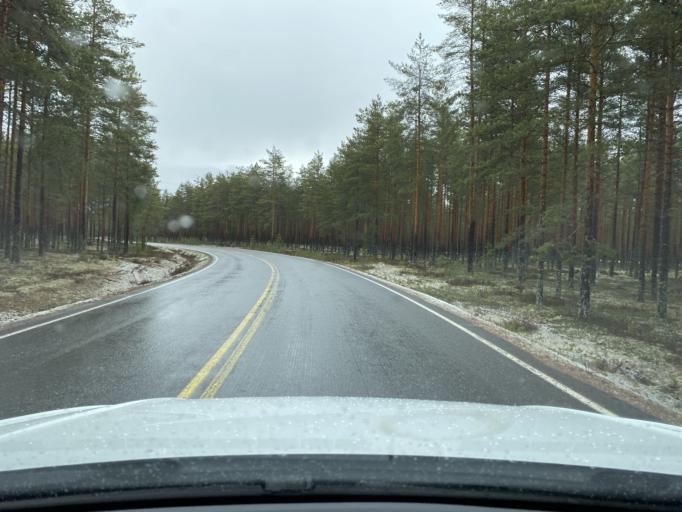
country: FI
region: Satakunta
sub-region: Pori
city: Vampula
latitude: 60.9675
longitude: 22.6804
